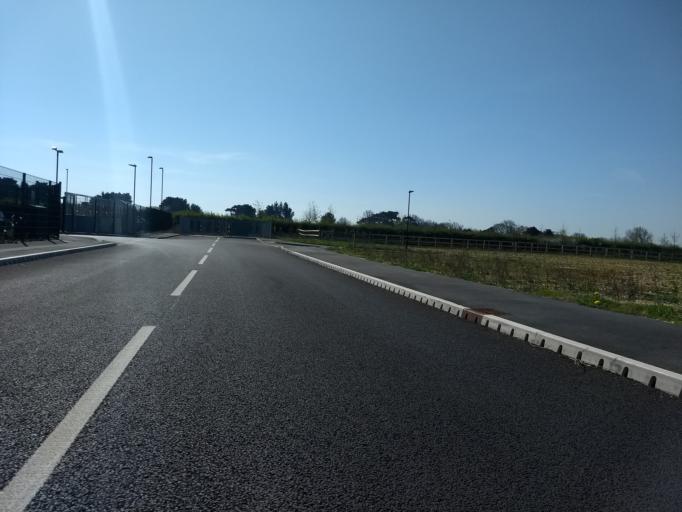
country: GB
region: England
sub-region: Isle of Wight
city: East Cowes
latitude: 50.7419
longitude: -1.2718
